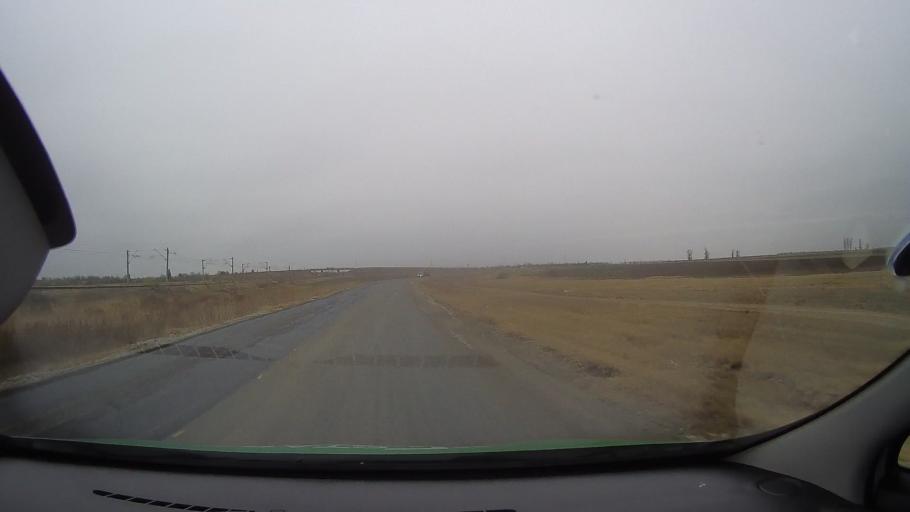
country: RO
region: Braila
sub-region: Comuna Baraganul
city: Baraganul
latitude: 44.8028
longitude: 27.5257
